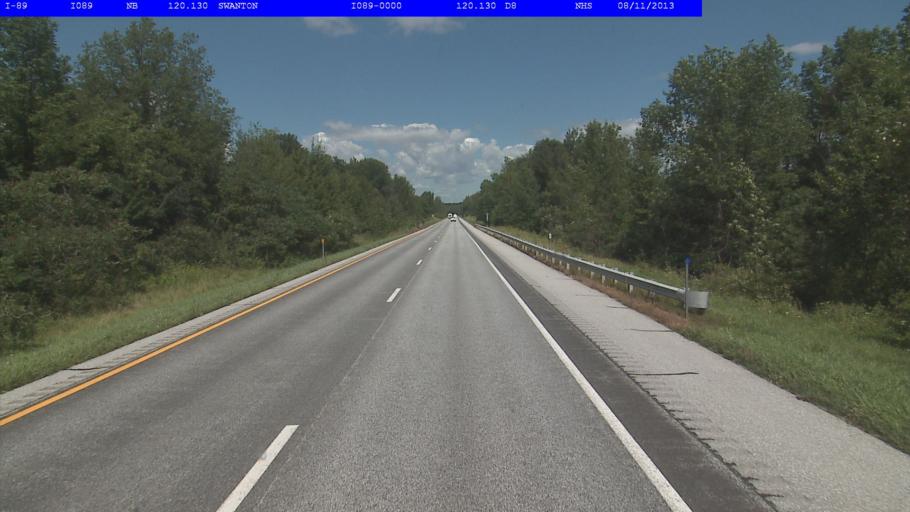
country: US
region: Vermont
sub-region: Franklin County
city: Swanton
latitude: 44.8790
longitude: -73.0834
